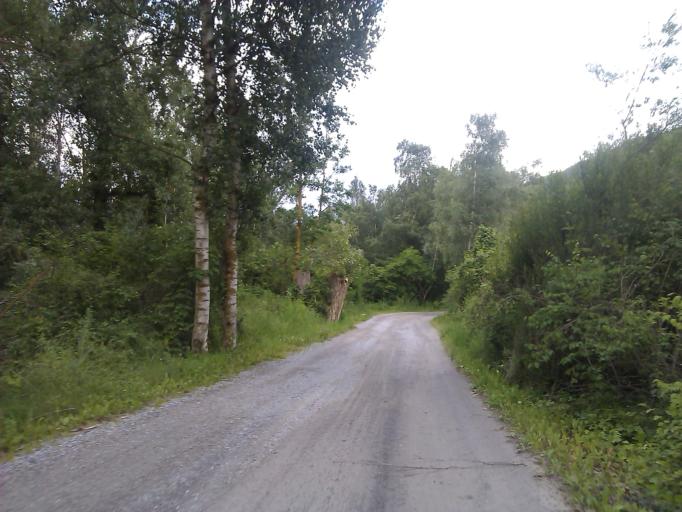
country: IT
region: Trentino-Alto Adige
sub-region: Bolzano
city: Prato Allo Stelvio
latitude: 46.6179
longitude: 10.6380
